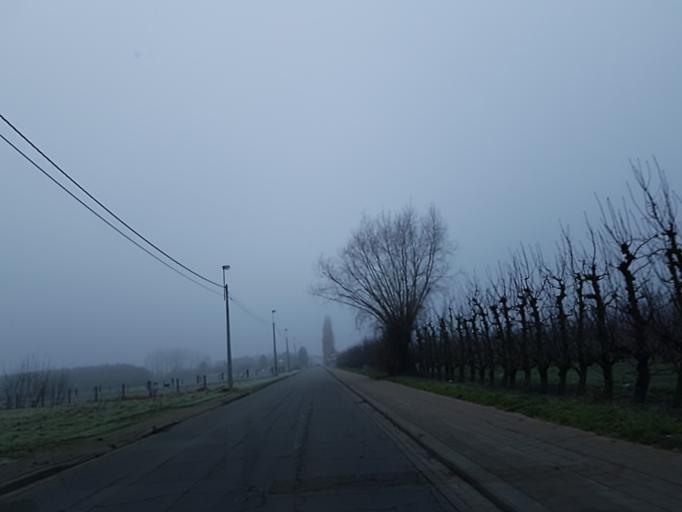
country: BE
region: Flanders
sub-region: Provincie Vlaams-Brabant
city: Kapelle-op-den-Bos
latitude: 50.9751
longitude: 4.3578
